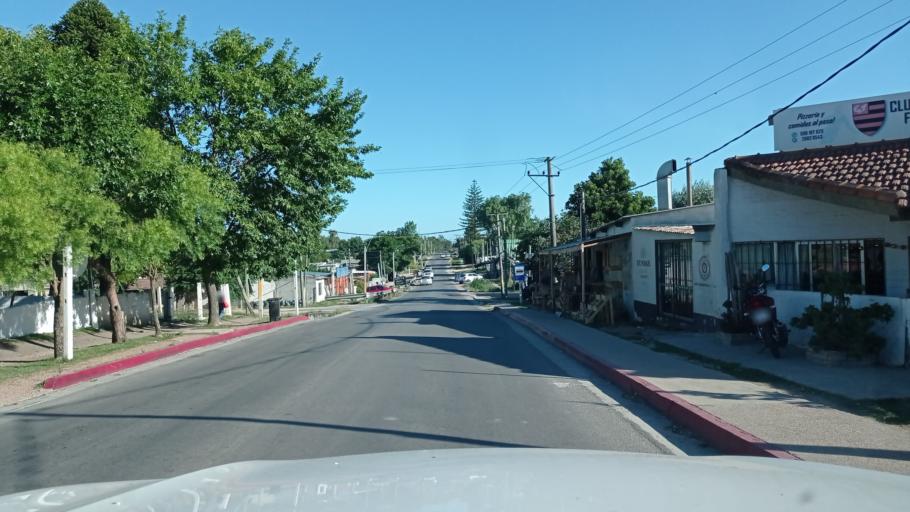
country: UY
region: Canelones
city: Colonia Nicolich
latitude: -34.8202
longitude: -56.0050
